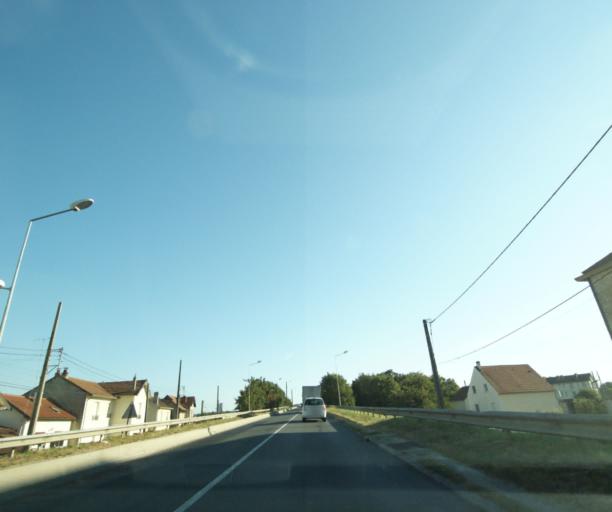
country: FR
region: Ile-de-France
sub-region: Departement de Seine-et-Marne
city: Montereau-Fault-Yonne
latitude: 48.3720
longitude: 2.9577
